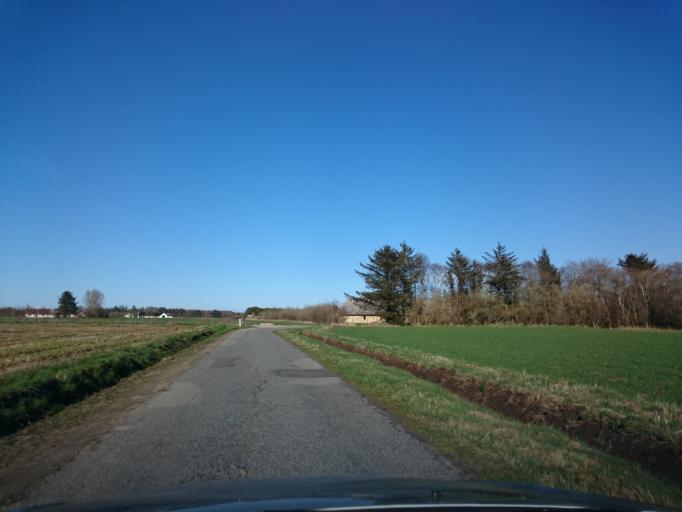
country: DK
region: North Denmark
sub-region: Hjorring Kommune
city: Hirtshals
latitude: 57.5551
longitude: 10.0637
